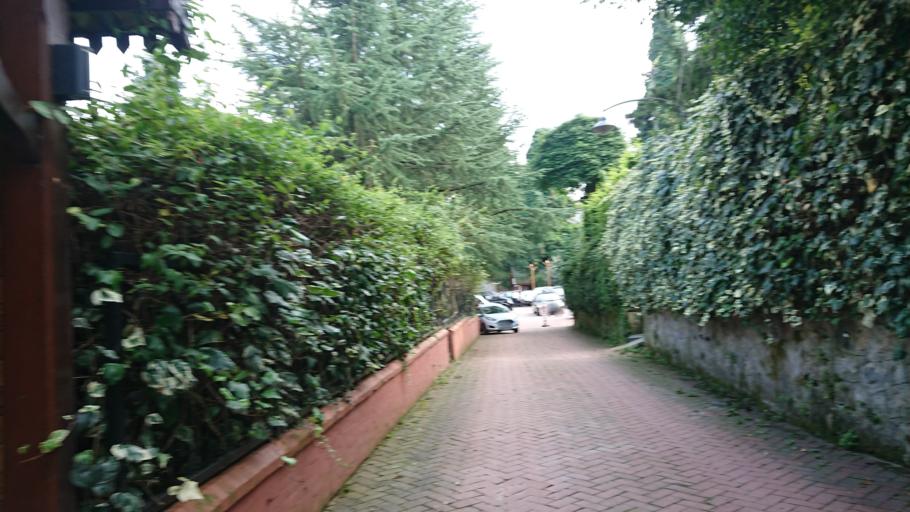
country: TR
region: Rize
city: Rize
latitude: 41.0215
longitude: 40.5111
